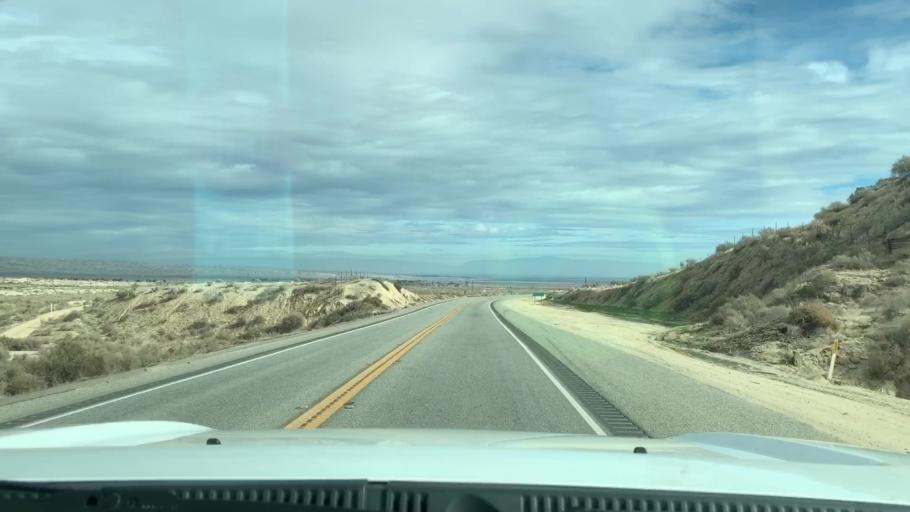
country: US
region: California
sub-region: Kern County
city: Ford City
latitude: 35.1854
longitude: -119.4492
